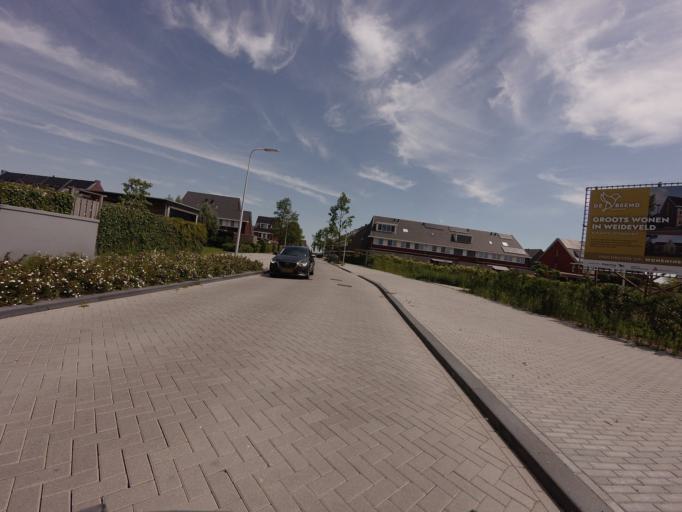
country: NL
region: South Holland
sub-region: Bodegraven-Reeuwijk
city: Bodegraven
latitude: 52.0760
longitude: 4.7626
